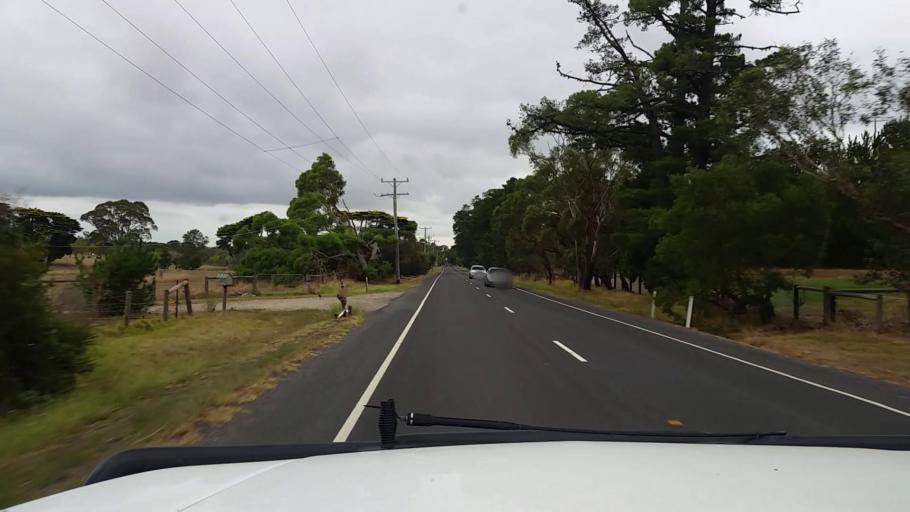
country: AU
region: Victoria
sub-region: Mornington Peninsula
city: Tyabb
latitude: -38.2535
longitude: 145.1468
